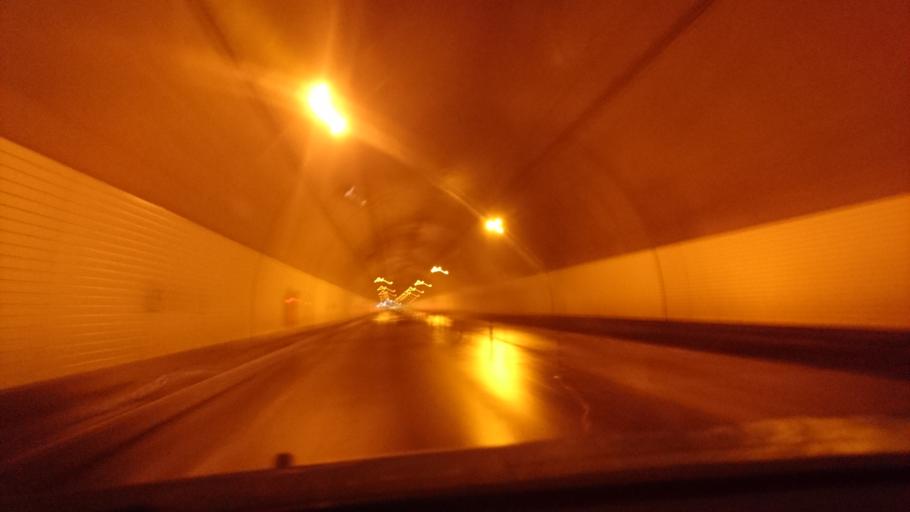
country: JP
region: Iwate
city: Miyako
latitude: 39.8542
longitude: 141.9439
